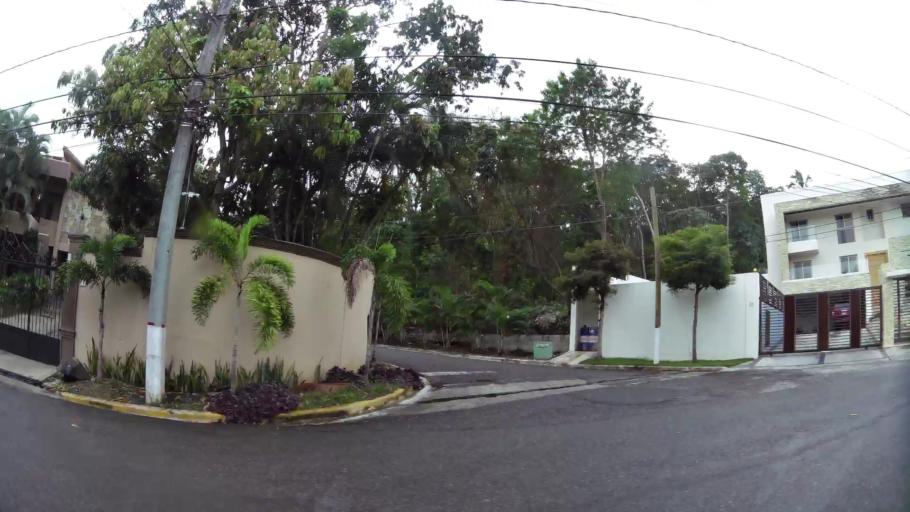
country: DO
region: Nacional
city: La Agustina
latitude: 18.5116
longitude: -69.9531
